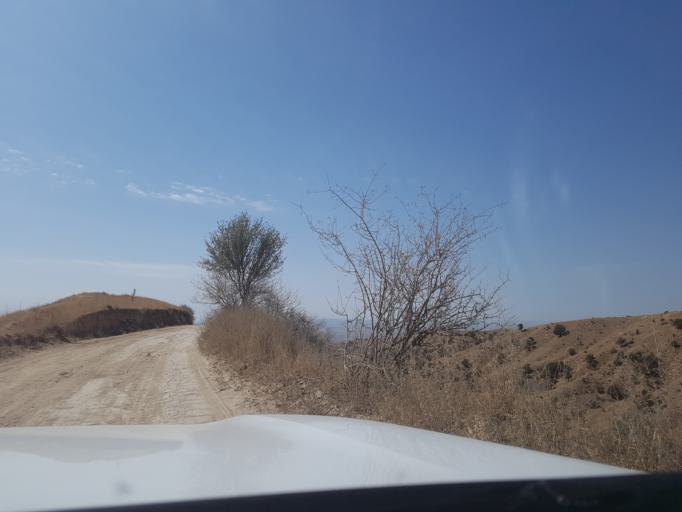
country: TM
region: Ahal
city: Baharly
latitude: 38.2958
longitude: 56.9356
